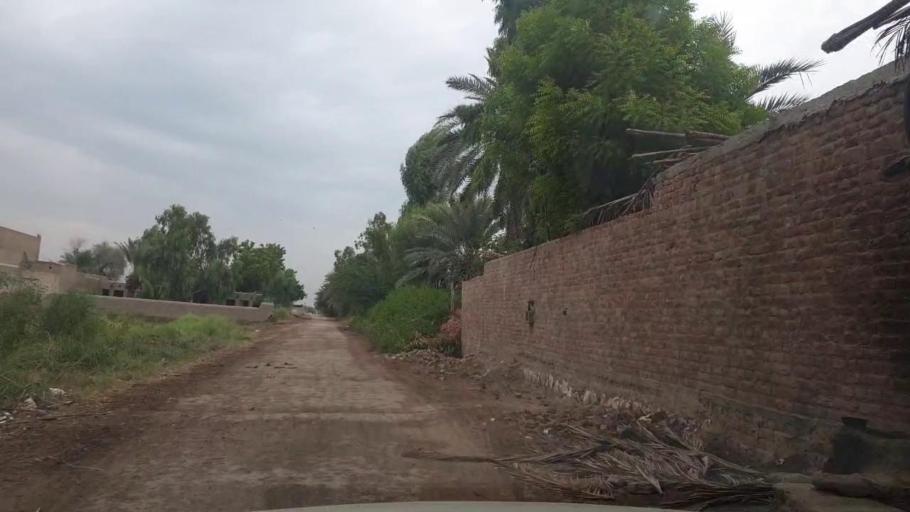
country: PK
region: Sindh
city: Khairpur
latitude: 27.5928
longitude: 68.8137
